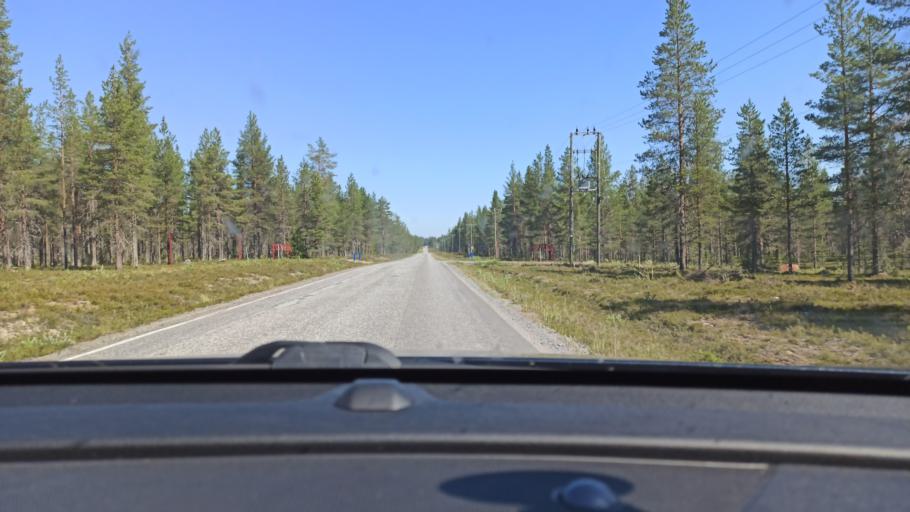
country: FI
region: Lapland
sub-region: Tunturi-Lappi
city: Kolari
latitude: 67.6465
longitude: 24.1603
